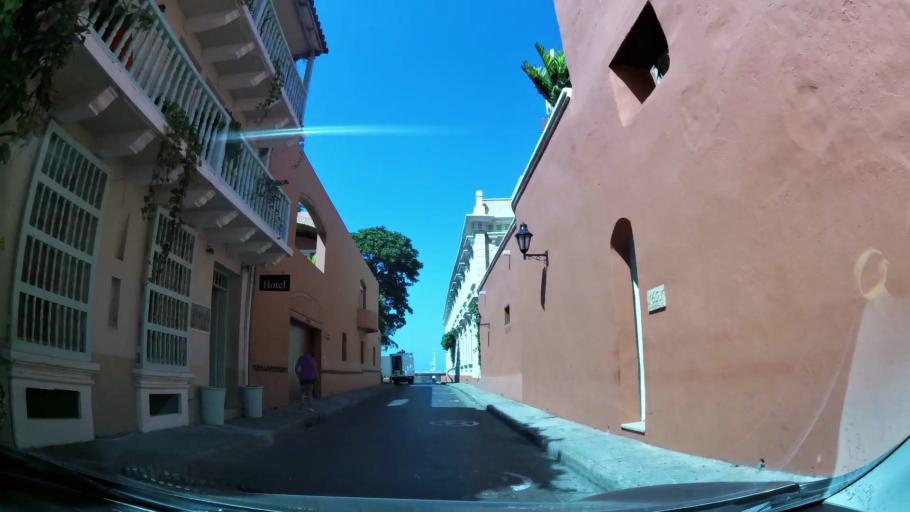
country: CO
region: Bolivar
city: Cartagena
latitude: 10.4283
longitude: -75.5483
